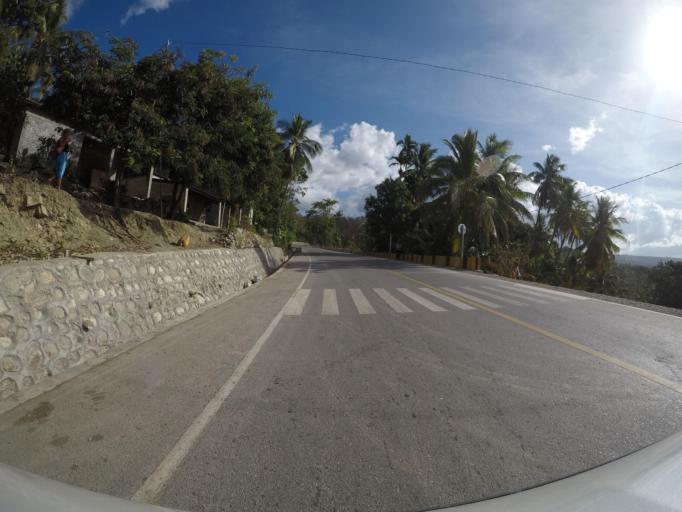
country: TL
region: Baucau
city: Baucau
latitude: -8.4556
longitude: 126.4724
